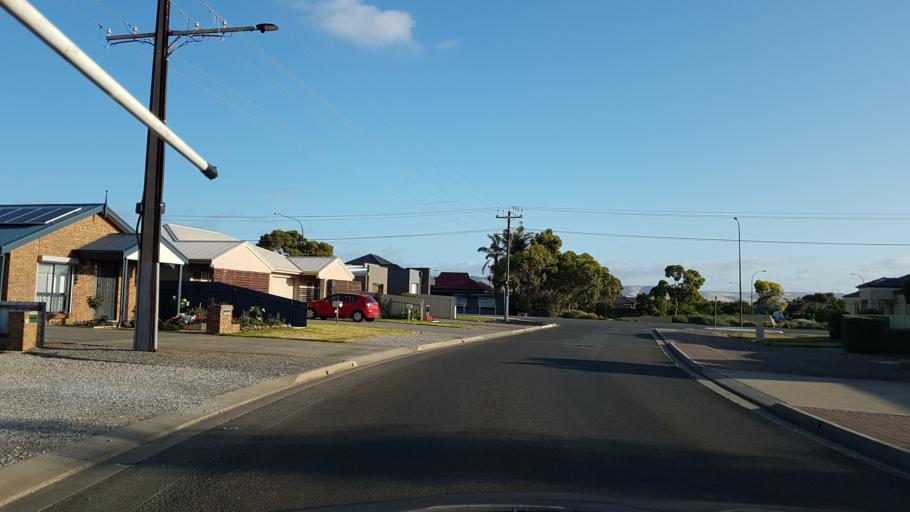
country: AU
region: South Australia
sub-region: Onkaparinga
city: Port Willunga
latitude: -35.2781
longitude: 138.4528
